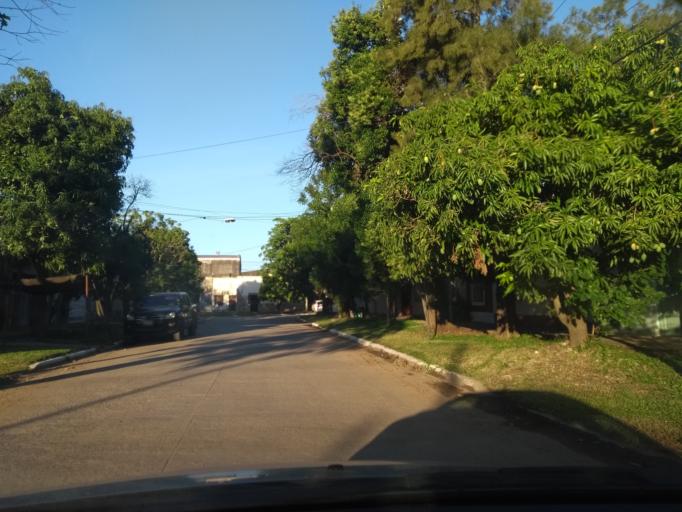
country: AR
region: Chaco
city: Barranqueras
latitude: -27.4838
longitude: -58.9424
